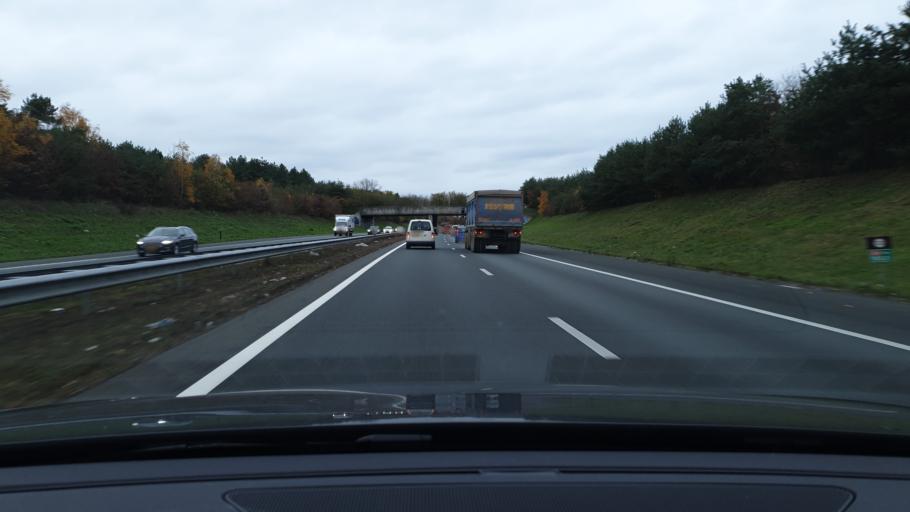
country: NL
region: North Brabant
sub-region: Gemeente Son en Breugel
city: Son
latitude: 51.5196
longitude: 5.4683
